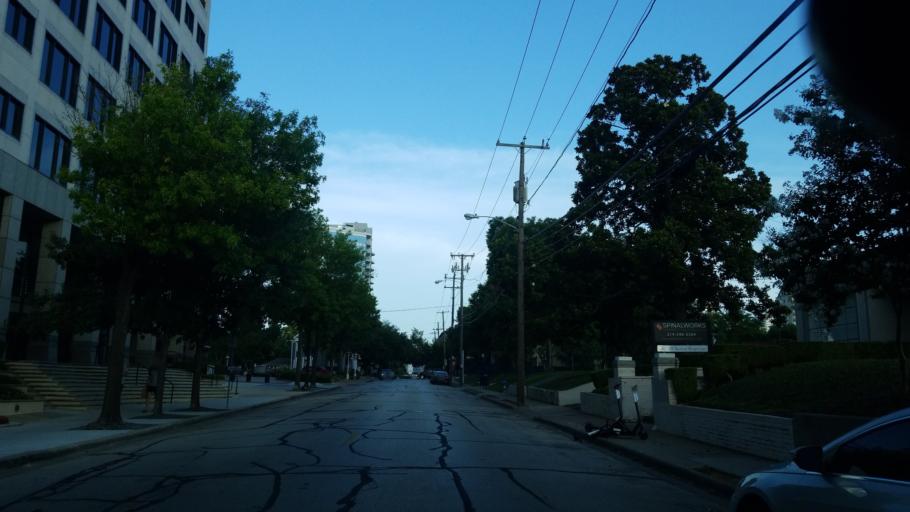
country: US
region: Texas
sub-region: Dallas County
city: Dallas
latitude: 32.7988
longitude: -96.8047
